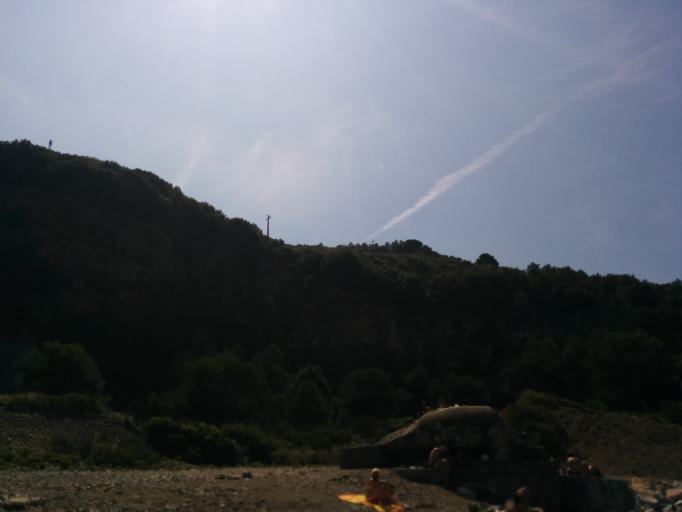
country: IT
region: Liguria
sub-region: Provincia di La Spezia
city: Portovenere
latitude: 44.0478
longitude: 9.8358
